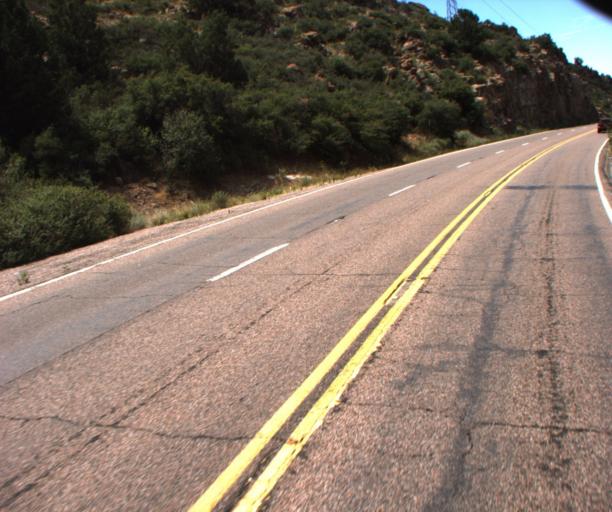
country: US
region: Arizona
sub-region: Pinal County
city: Superior
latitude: 33.3361
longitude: -111.0237
